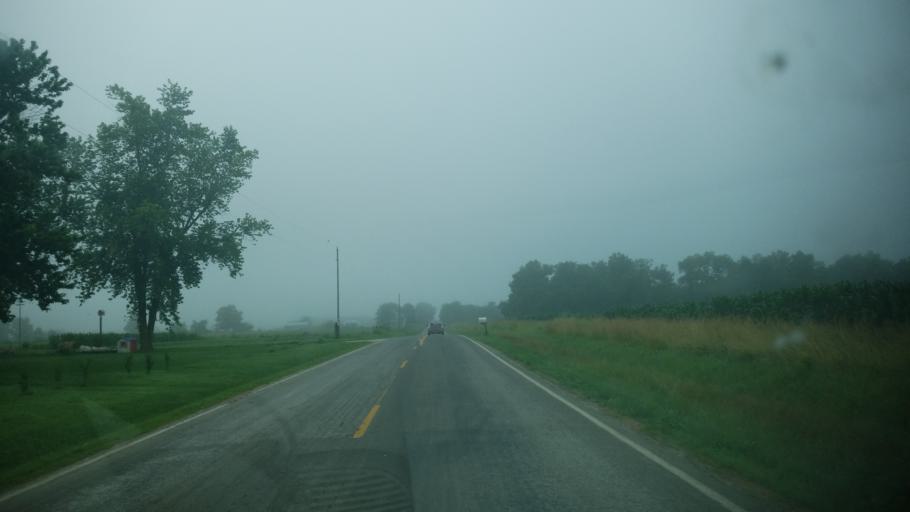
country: US
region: Missouri
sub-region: Audrain County
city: Vandalia
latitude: 39.3257
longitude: -91.3451
